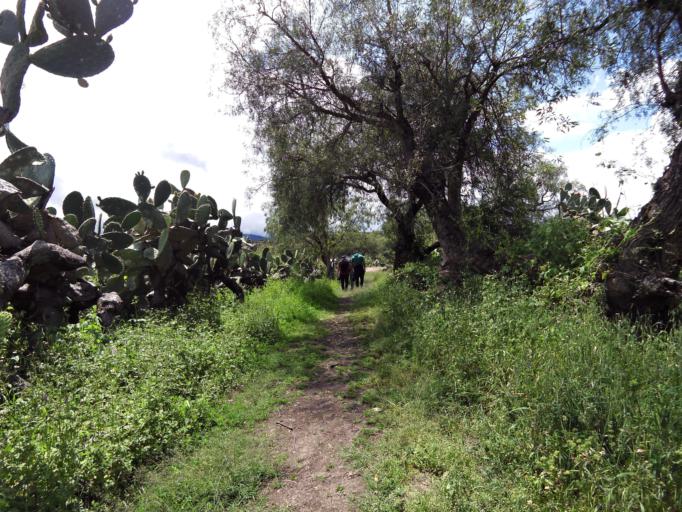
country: PE
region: Ayacucho
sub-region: Provincia de Huamanga
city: Pacaycasa
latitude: -13.0666
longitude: -74.1907
